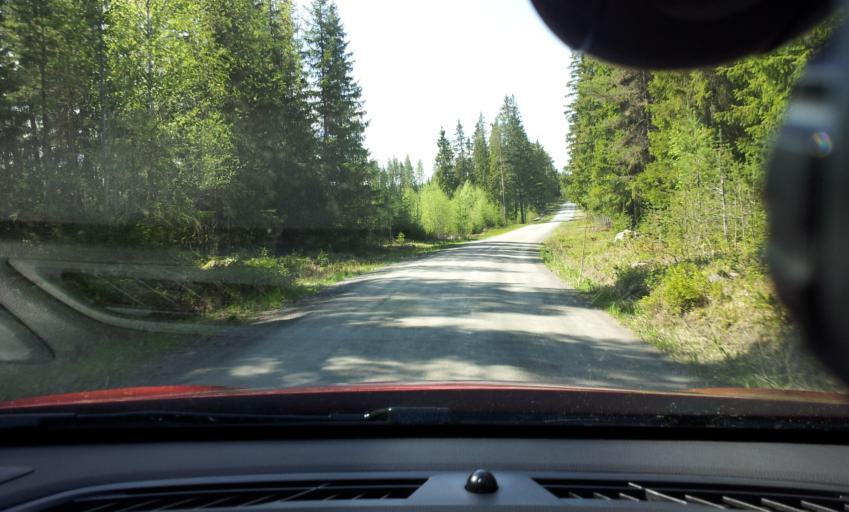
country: SE
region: Jaemtland
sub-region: Bergs Kommun
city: Hoverberg
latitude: 62.9526
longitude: 14.5351
